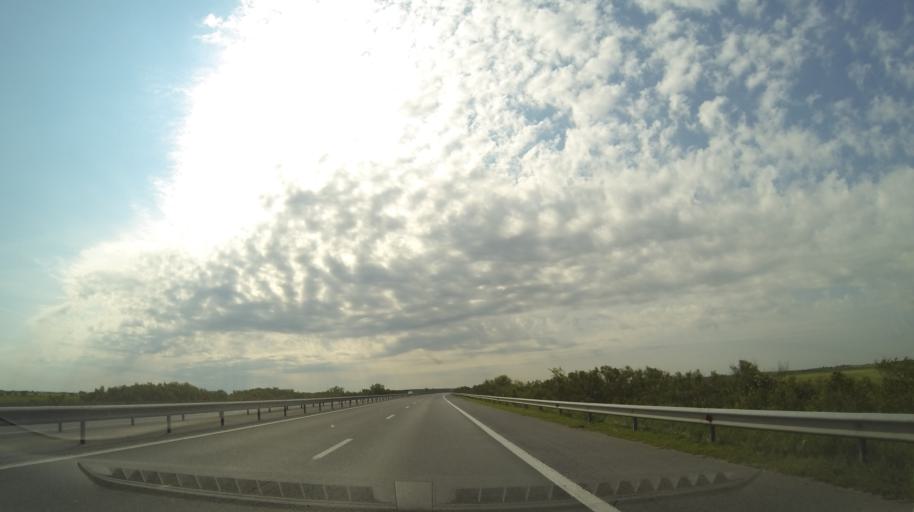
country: RO
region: Arges
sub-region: Comuna Cateasca
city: Cateasca
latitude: 44.7508
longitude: 25.0936
